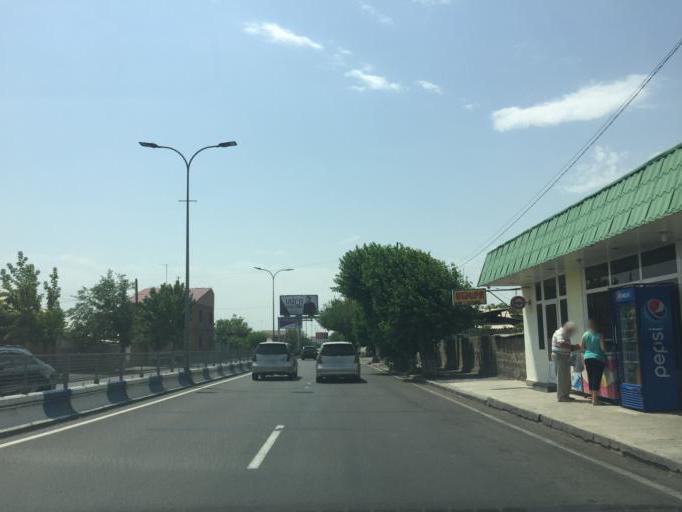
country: AM
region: Armavir
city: Mertsavan
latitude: 40.1643
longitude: 44.4108
